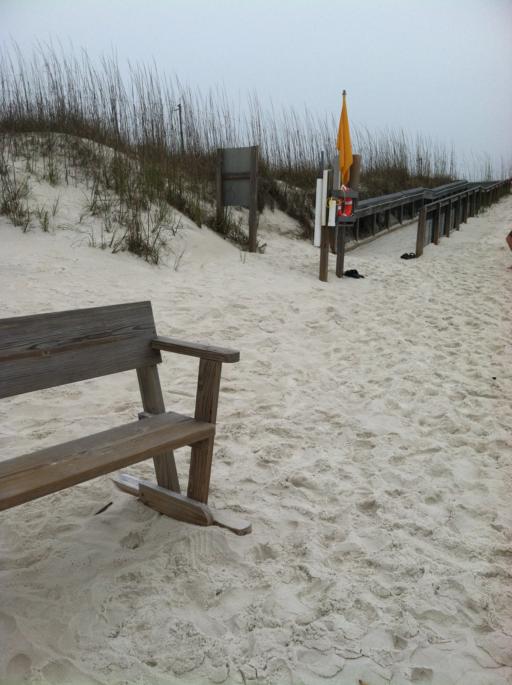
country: US
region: Florida
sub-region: Gulf County
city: Port Saint Joe
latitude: 29.7748
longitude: -85.4074
